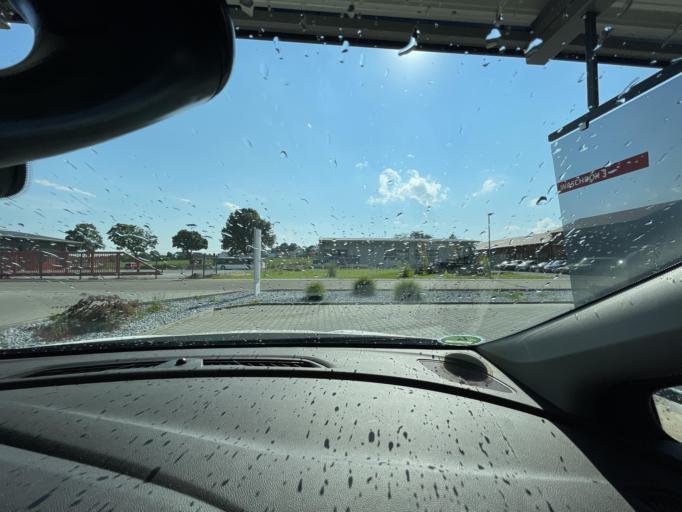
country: DE
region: Bavaria
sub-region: Swabia
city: Hollenbach
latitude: 48.4930
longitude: 11.0914
